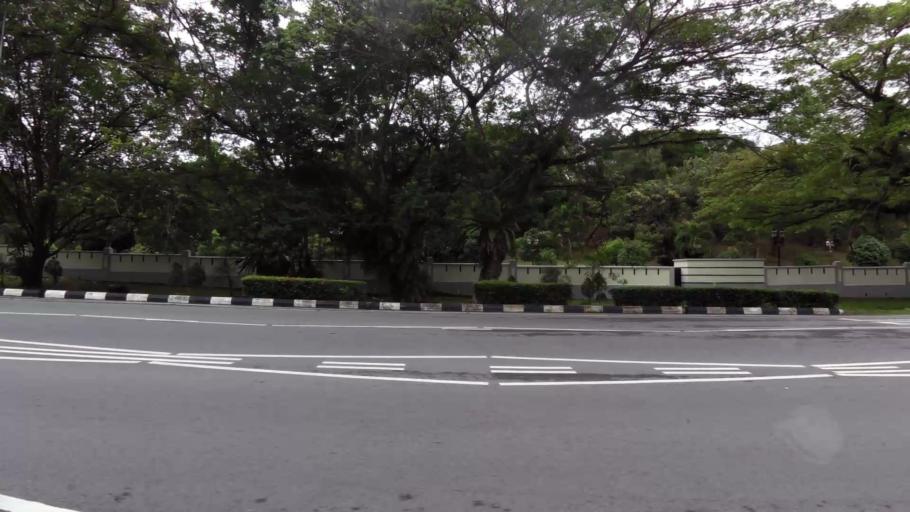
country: BN
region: Brunei and Muara
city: Bandar Seri Begawan
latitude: 4.9076
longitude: 114.9318
